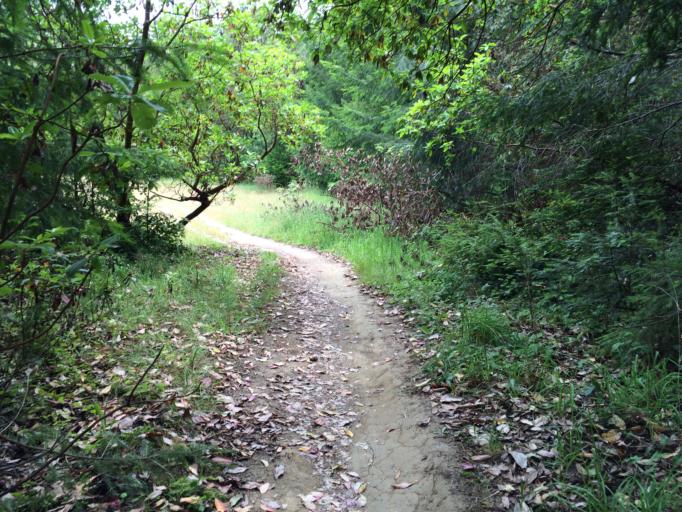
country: US
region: California
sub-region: Santa Cruz County
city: Felton
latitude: 37.0182
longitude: -122.0760
